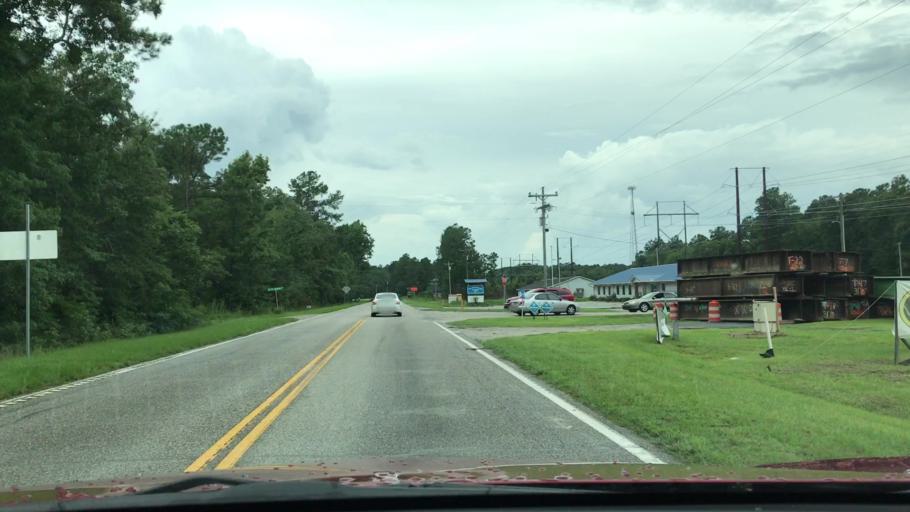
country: US
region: South Carolina
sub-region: Georgetown County
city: Murrells Inlet
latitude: 33.6516
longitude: -79.1670
